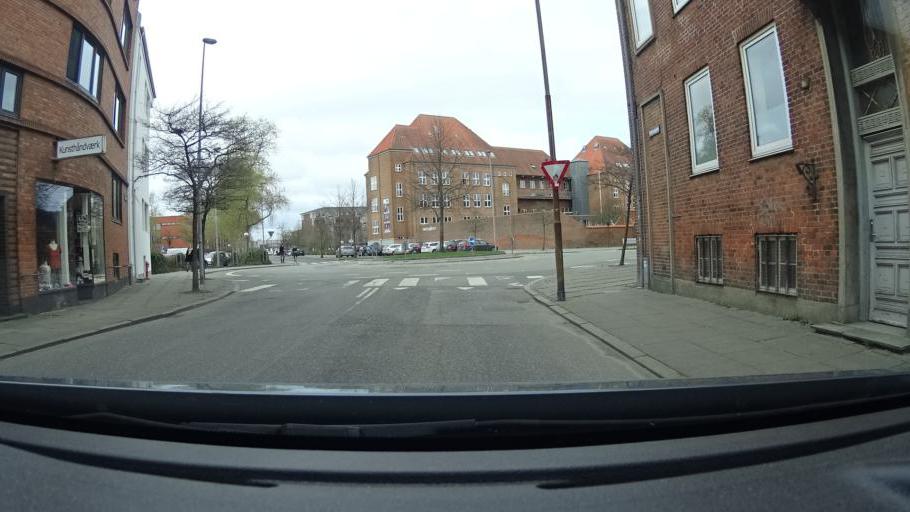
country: DK
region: South Denmark
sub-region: Vejle Kommune
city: Vejle
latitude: 55.7119
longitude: 9.5292
